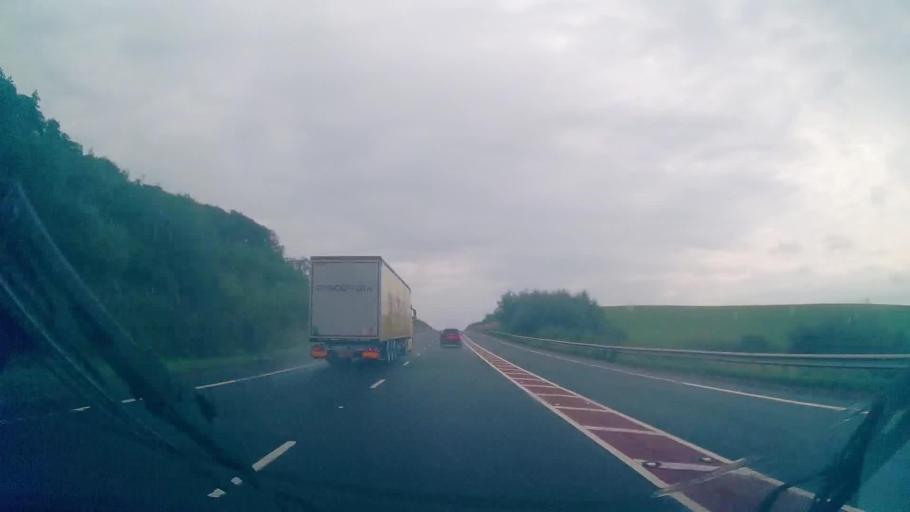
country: GB
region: Scotland
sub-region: Dumfries and Galloway
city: Lockerbie
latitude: 55.0257
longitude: -3.3827
